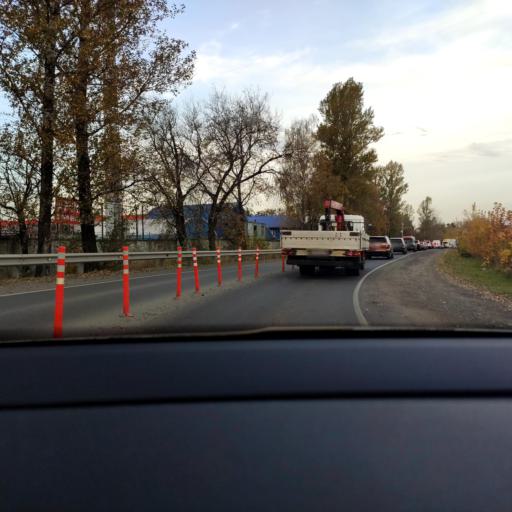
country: RU
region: Moskovskaya
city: Cherkizovo
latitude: 55.9686
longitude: 37.7637
